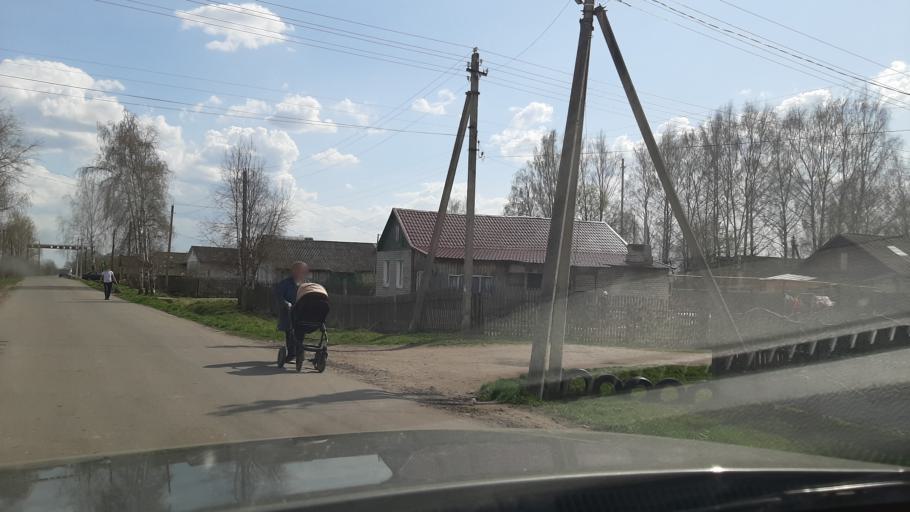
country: RU
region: Ivanovo
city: Privolzhsk
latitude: 57.3306
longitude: 41.2340
